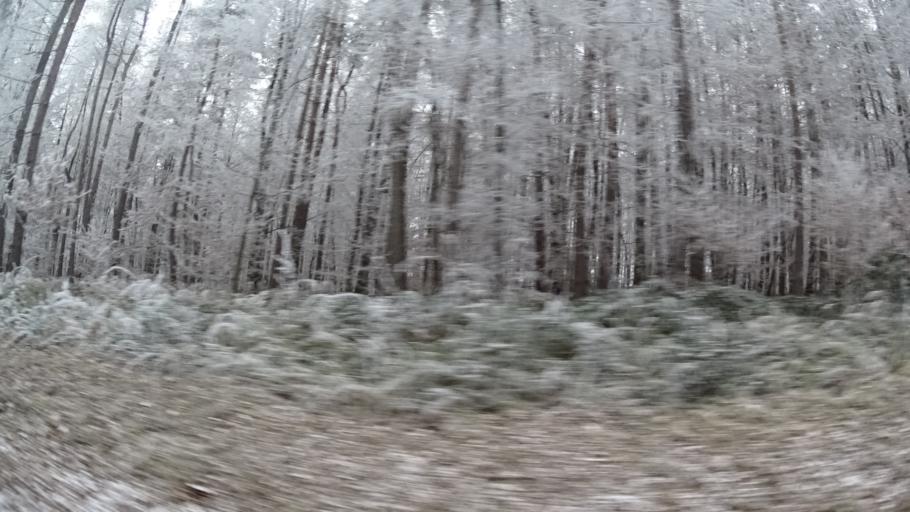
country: DE
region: Bavaria
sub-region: Regierungsbezirk Unterfranken
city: Johannesberg
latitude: 50.0444
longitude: 9.0931
